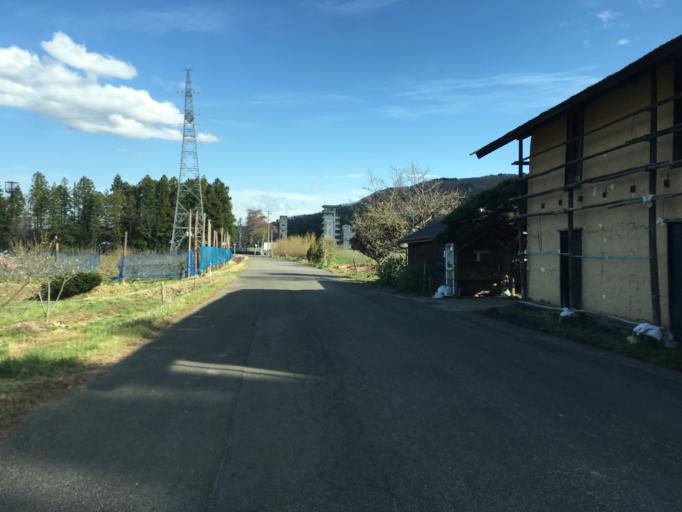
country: JP
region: Fukushima
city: Fukushima-shi
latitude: 37.7129
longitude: 140.3700
